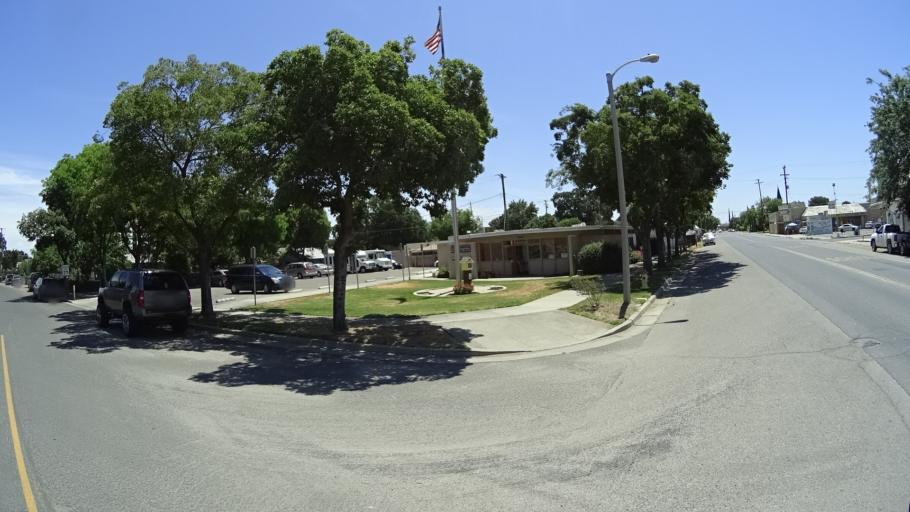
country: US
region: California
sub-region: Kings County
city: Armona
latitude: 36.3147
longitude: -119.7090
